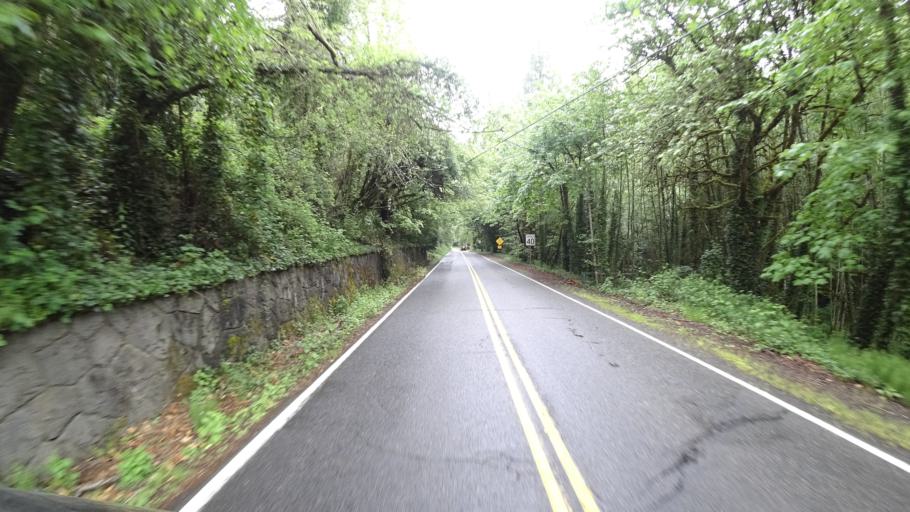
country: US
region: Oregon
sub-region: Washington County
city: West Haven-Sylvan
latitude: 45.5351
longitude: -122.7410
